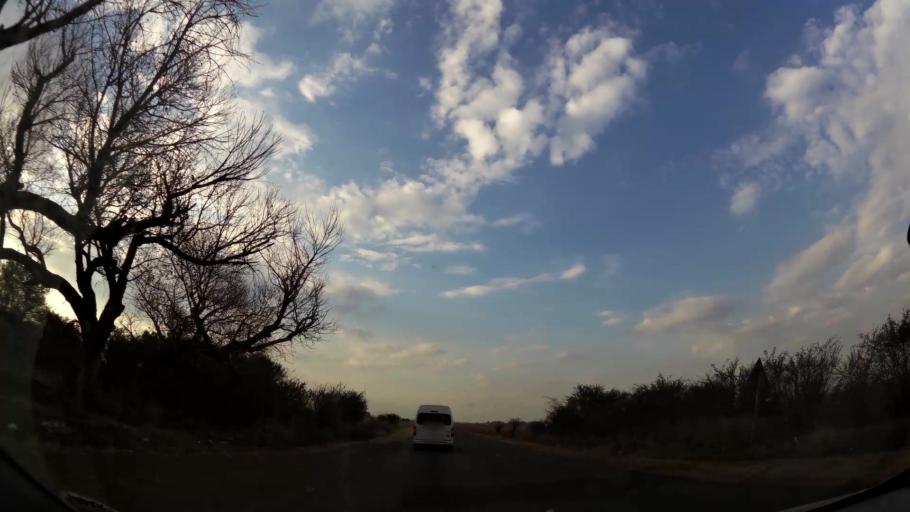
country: ZA
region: Gauteng
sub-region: Sedibeng District Municipality
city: Vanderbijlpark
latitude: -26.6302
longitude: 27.8091
